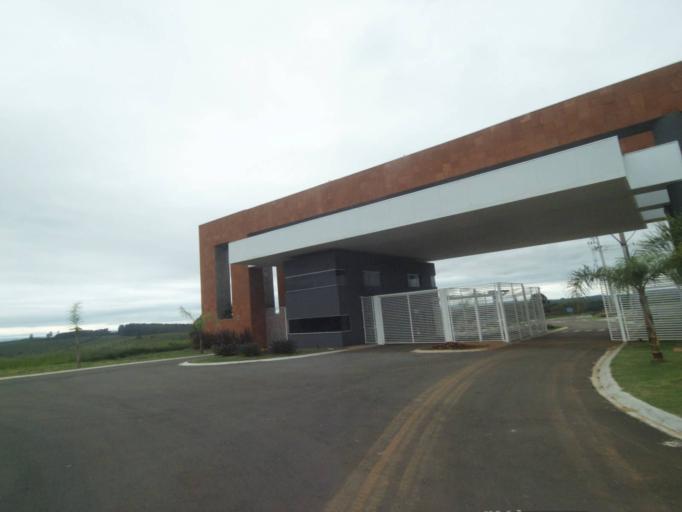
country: BR
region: Parana
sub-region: Telemaco Borba
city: Telemaco Borba
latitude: -24.3856
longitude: -50.6752
